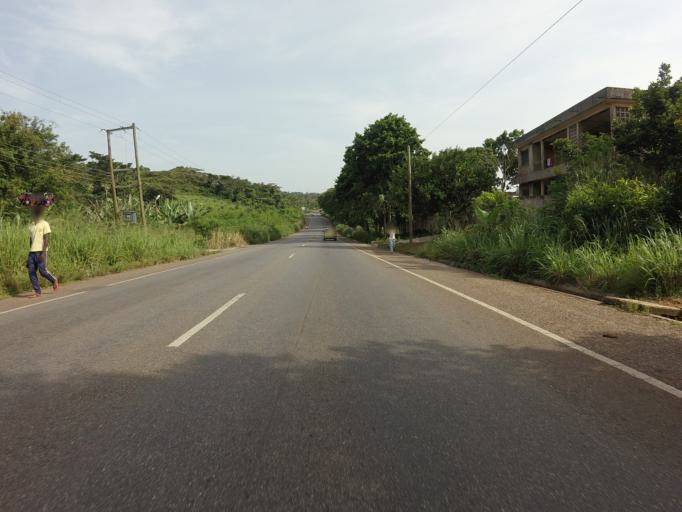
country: GH
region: Eastern
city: Aburi
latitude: 5.8960
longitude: -0.1502
